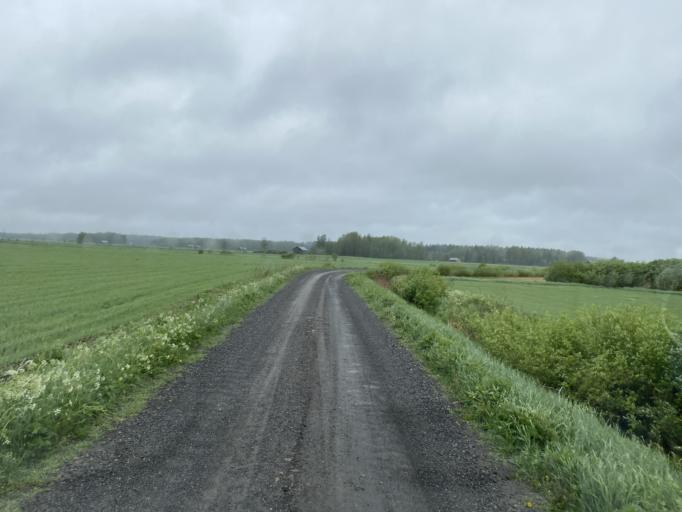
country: FI
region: Pirkanmaa
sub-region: Etelae-Pirkanmaa
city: Urjala
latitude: 60.9605
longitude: 23.5955
